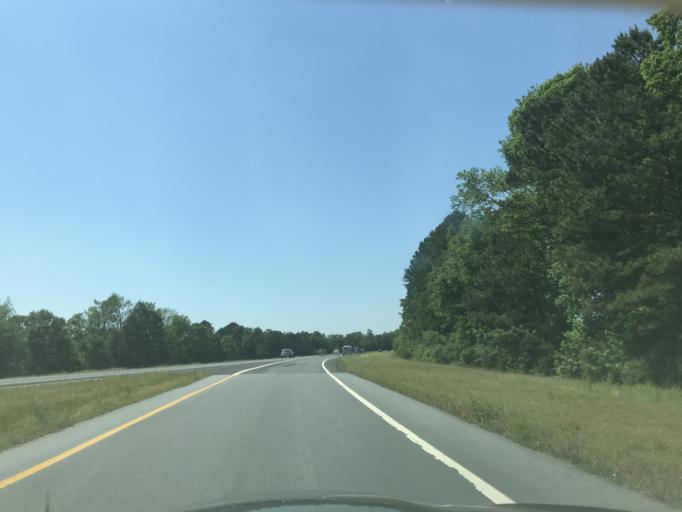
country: US
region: North Carolina
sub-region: Johnston County
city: Benson
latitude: 35.3308
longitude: -78.4518
